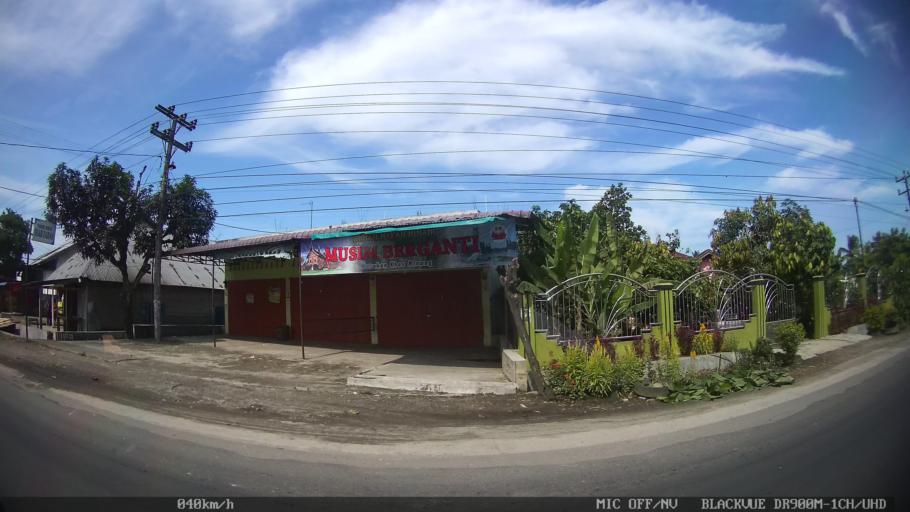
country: ID
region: North Sumatra
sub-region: Kabupaten Langkat
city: Stabat
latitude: 3.6922
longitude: 98.5085
